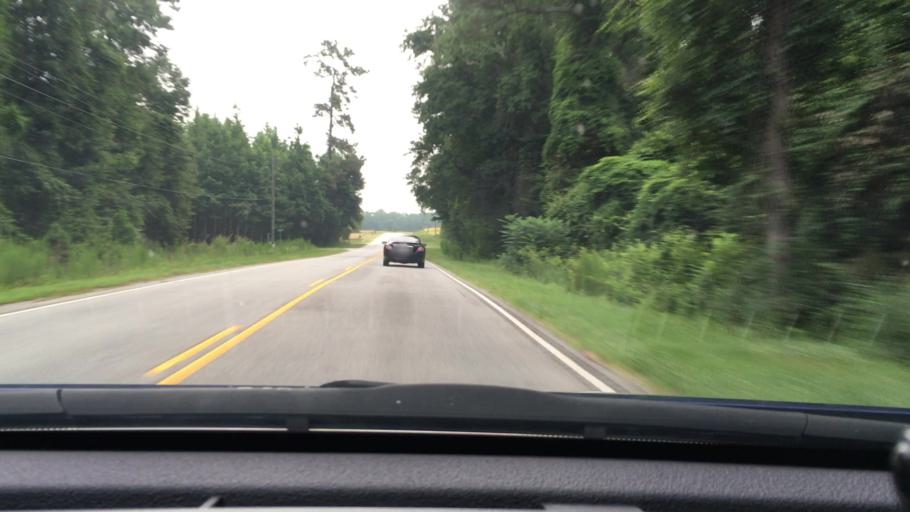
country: US
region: South Carolina
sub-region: Florence County
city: Timmonsville
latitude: 34.1932
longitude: -80.0412
